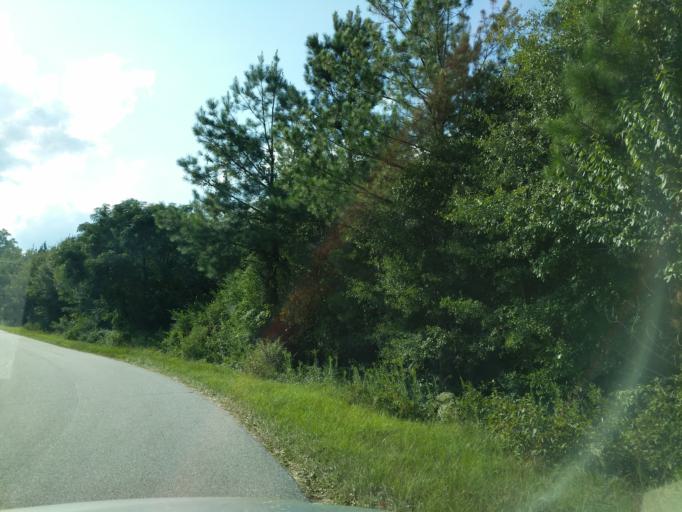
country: US
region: South Carolina
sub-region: Greenville County
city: Fountain Inn
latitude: 34.5921
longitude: -82.1750
